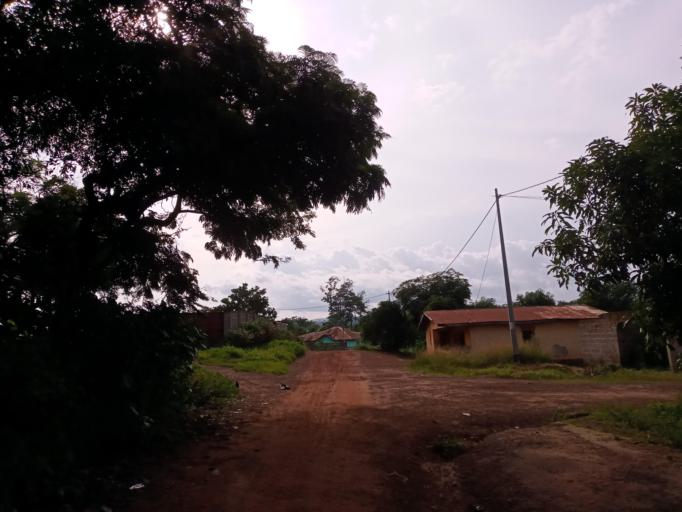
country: SL
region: Northern Province
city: Bumbuna
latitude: 9.0421
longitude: -11.7550
